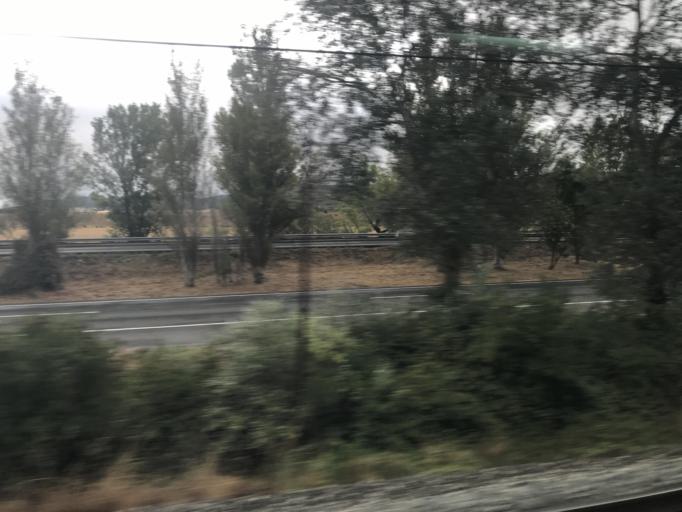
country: ES
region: Basque Country
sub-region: Provincia de Alava
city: Arminon
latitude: 42.7555
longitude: -2.8352
